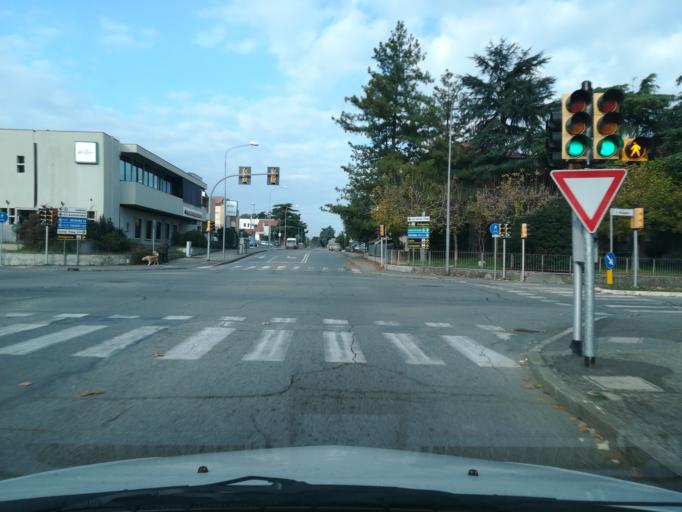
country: IT
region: Emilia-Romagna
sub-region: Provincia di Bologna
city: Imola
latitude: 44.3641
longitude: 11.7158
